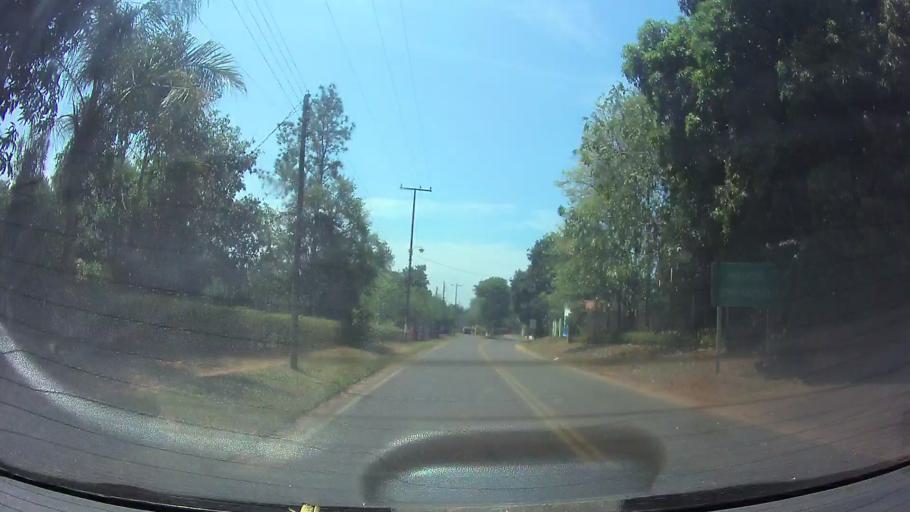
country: PY
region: Central
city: Ita
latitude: -25.4300
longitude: -57.3969
